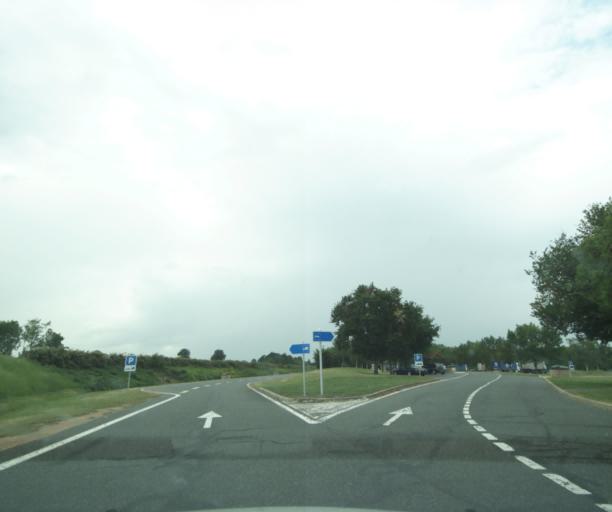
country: FR
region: Auvergne
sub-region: Departement de l'Allier
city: Vallon-en-Sully
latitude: 46.5165
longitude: 2.5825
